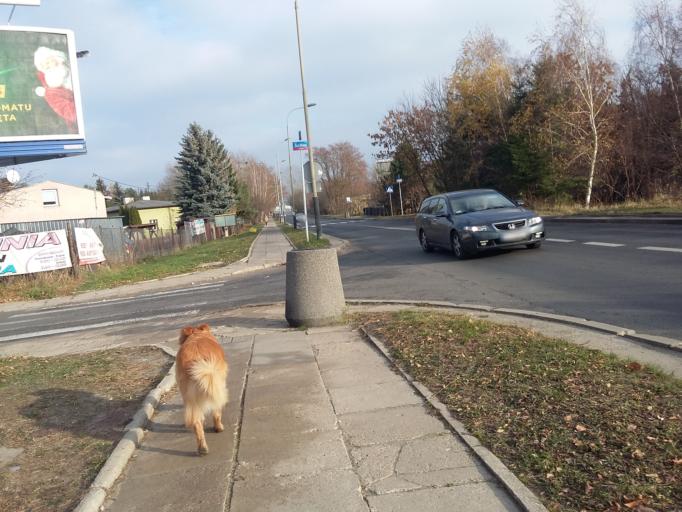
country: PL
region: Lodz Voivodeship
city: Lodz
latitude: 51.7384
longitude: 19.4124
